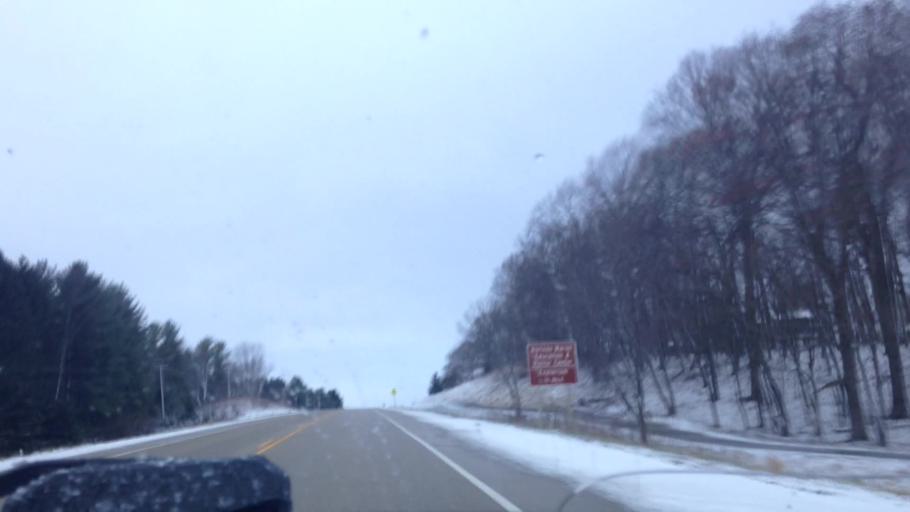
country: US
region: Wisconsin
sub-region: Dodge County
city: Horicon
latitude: 43.4782
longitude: -88.5919
